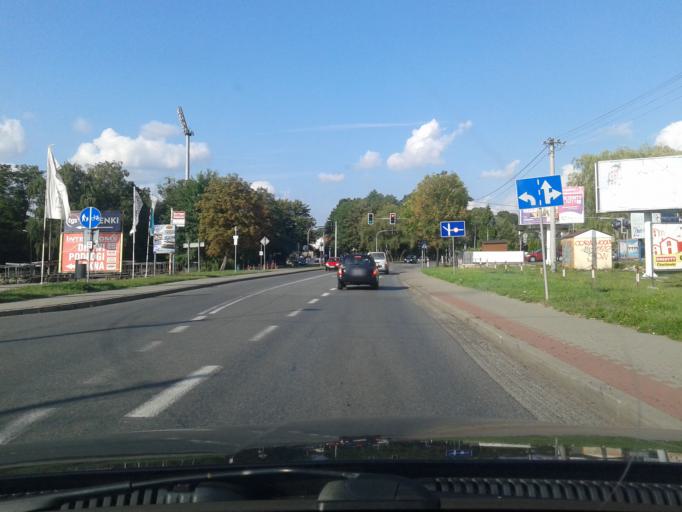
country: PL
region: Silesian Voivodeship
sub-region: Powiat wodzislawski
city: Wodzislaw Slaski
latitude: 49.9966
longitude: 18.4582
